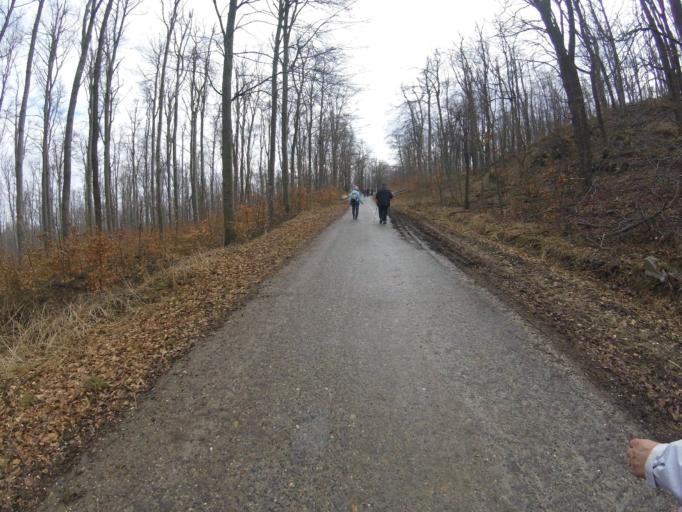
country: HU
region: Pest
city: Pilisszanto
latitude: 47.6976
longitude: 18.8620
